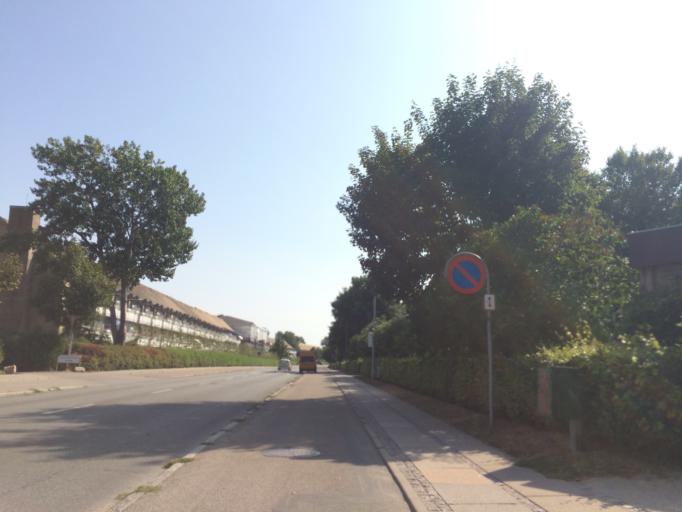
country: DK
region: Capital Region
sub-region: Hvidovre Kommune
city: Hvidovre
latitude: 55.6408
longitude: 12.4699
